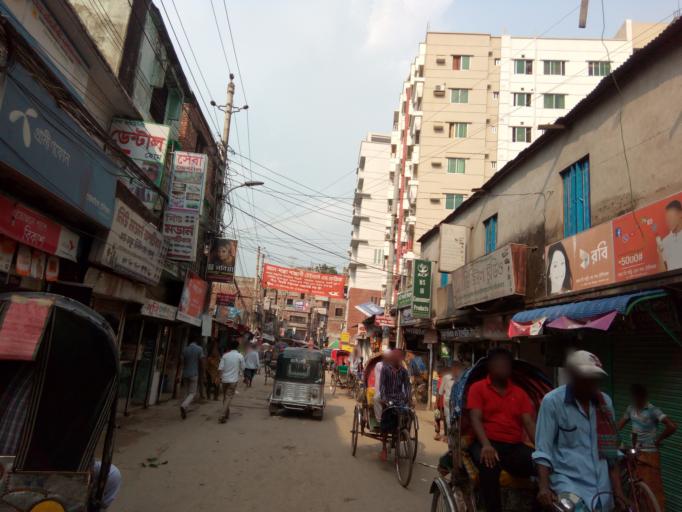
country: BD
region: Dhaka
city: Paltan
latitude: 23.7227
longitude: 90.4299
